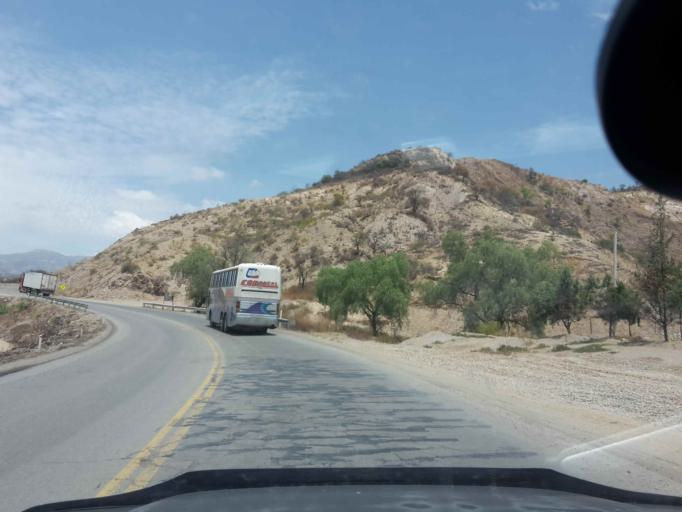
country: BO
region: Cochabamba
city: Sipe Sipe
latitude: -17.5465
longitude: -66.3409
